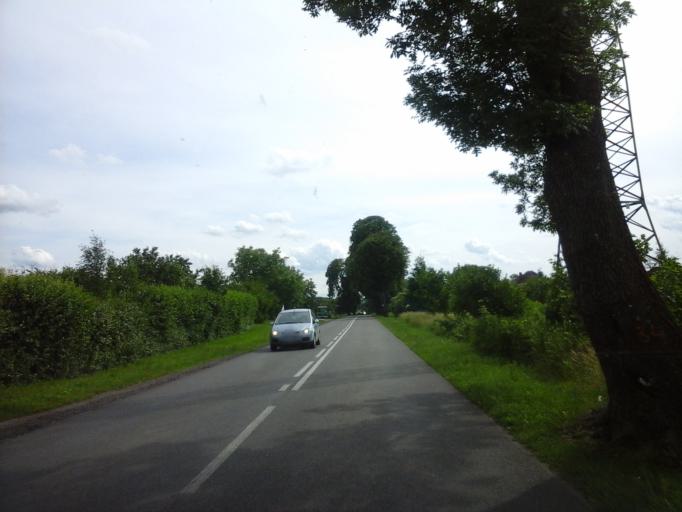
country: PL
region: West Pomeranian Voivodeship
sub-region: Powiat lobeski
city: Wegorzyno
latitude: 53.5472
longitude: 15.5631
